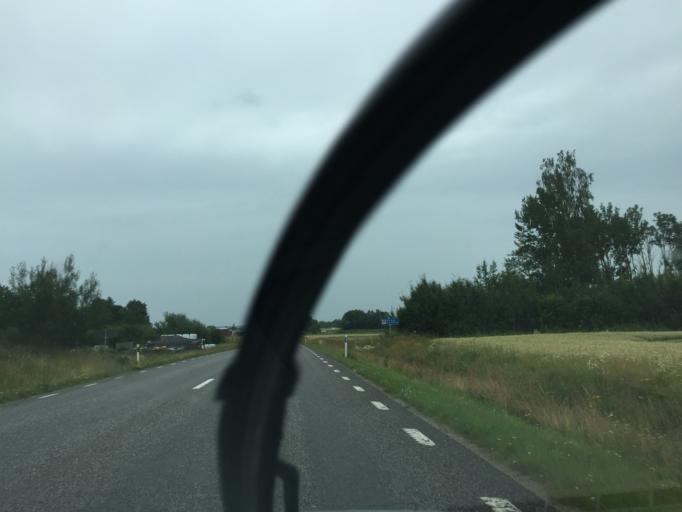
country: SE
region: OErebro
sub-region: Kumla Kommun
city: Hallabrottet
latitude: 59.1807
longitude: 15.2557
